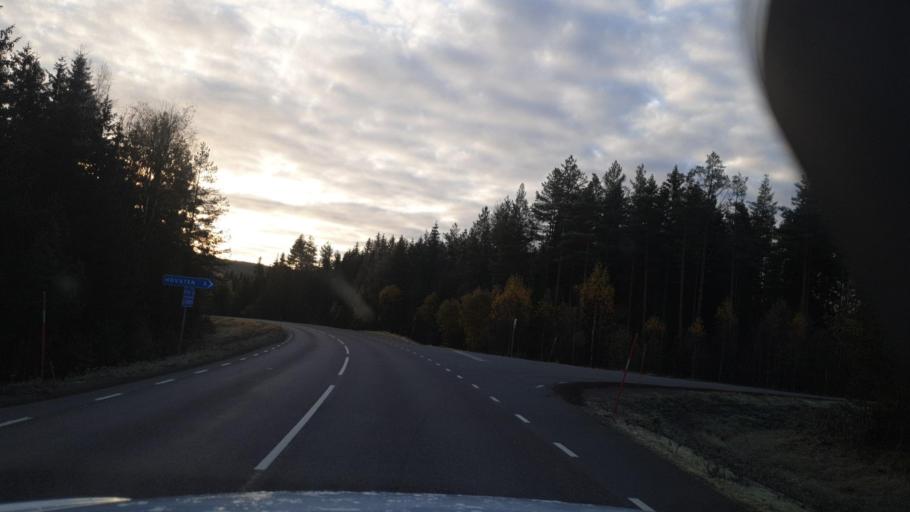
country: SE
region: Vaermland
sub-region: Eda Kommun
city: Amotfors
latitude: 59.7312
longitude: 12.1717
